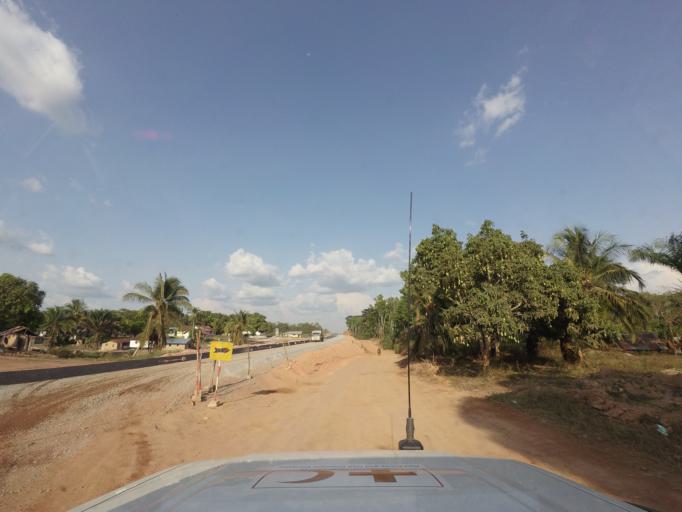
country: LR
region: Bong
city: Gbarnga
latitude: 7.0404
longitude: -9.5435
